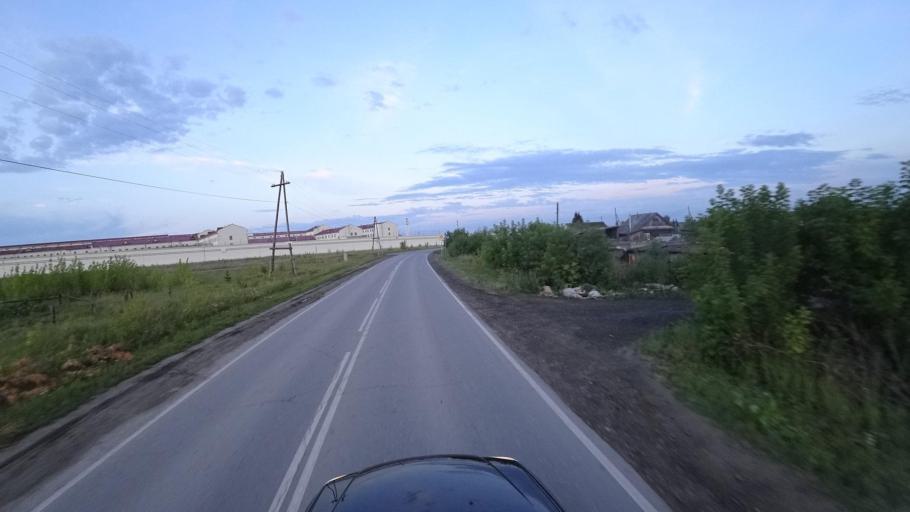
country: RU
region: Sverdlovsk
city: Kamyshlov
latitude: 56.8566
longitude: 62.7329
